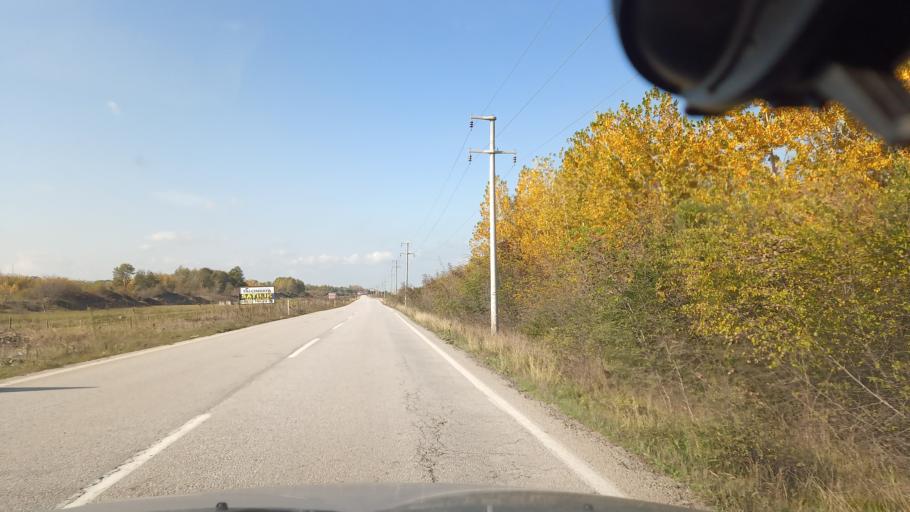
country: TR
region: Sakarya
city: Karasu
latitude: 41.1212
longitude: 30.5855
